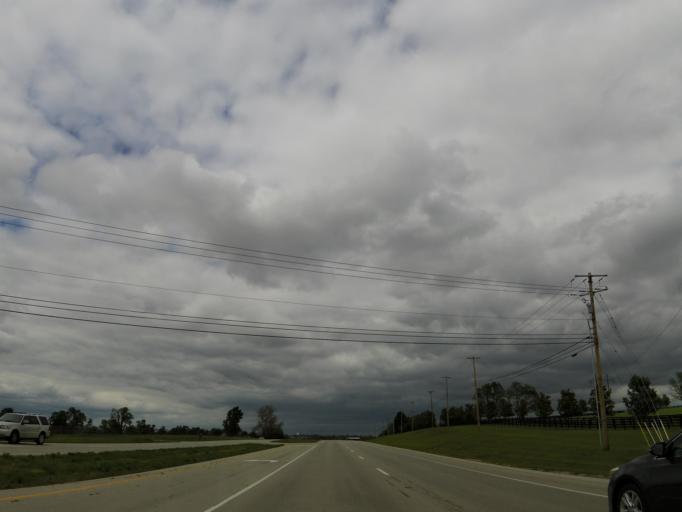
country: US
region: Kentucky
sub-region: Scott County
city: Georgetown
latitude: 38.1764
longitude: -84.5973
